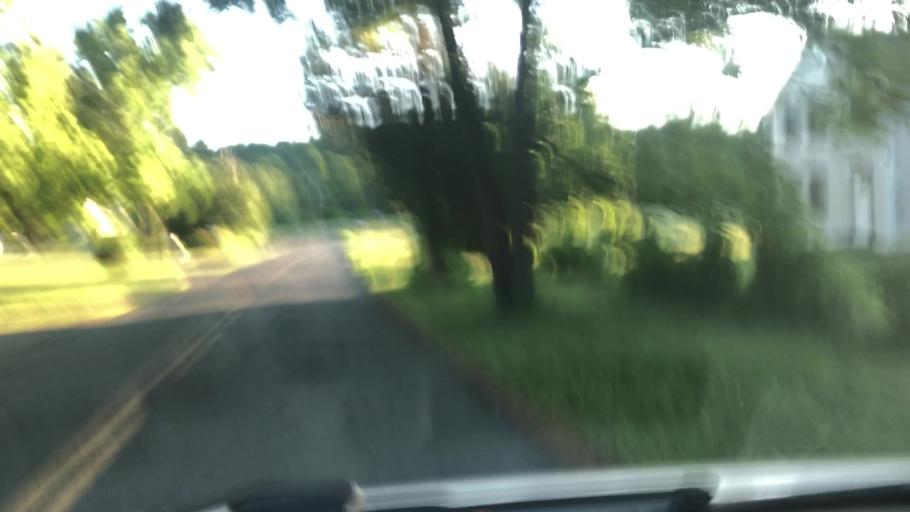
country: US
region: Massachusetts
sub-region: Hampshire County
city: Easthampton
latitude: 42.2775
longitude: -72.7163
